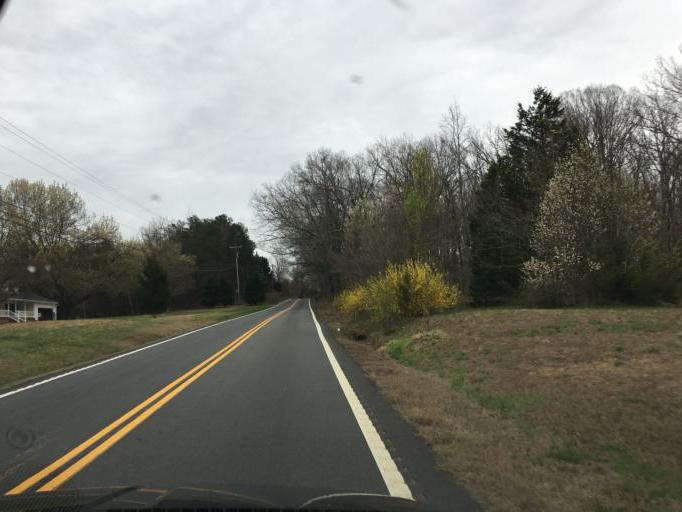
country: US
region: South Carolina
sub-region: Greenville County
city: Berea
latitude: 34.9229
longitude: -82.4828
